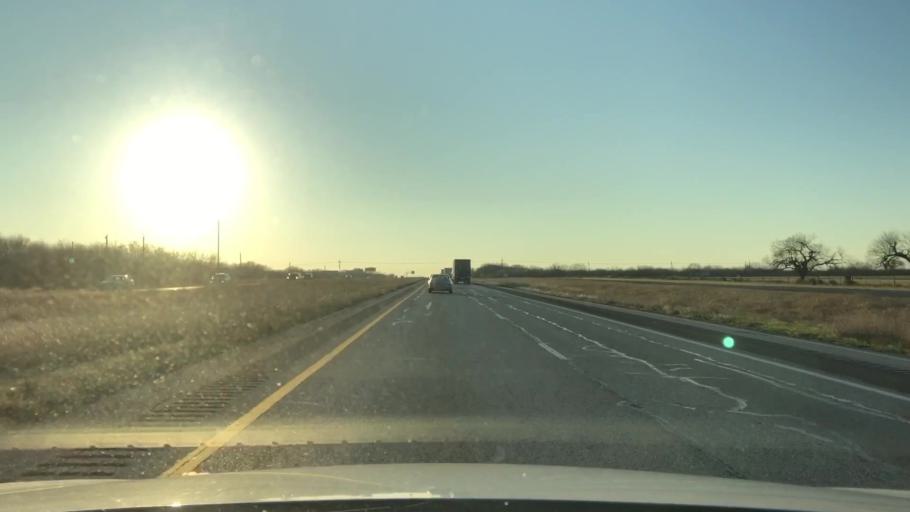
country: US
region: Texas
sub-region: Guadalupe County
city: Seguin
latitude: 29.6028
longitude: -97.9024
